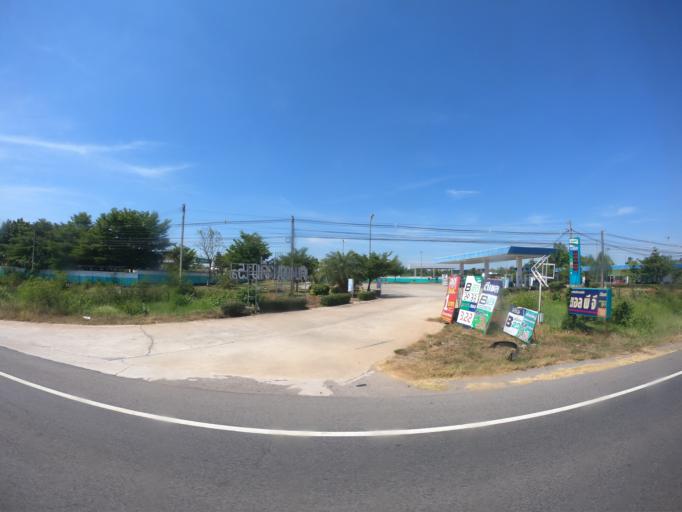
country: TH
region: Khon Kaen
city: Phon
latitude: 15.7535
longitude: 102.6040
